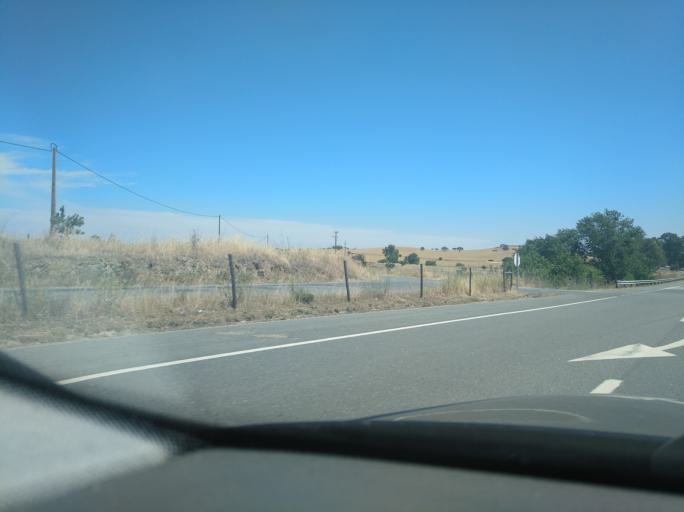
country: PT
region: Beja
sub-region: Castro Verde
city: Castro Verde
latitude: 37.6858
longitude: -8.0841
